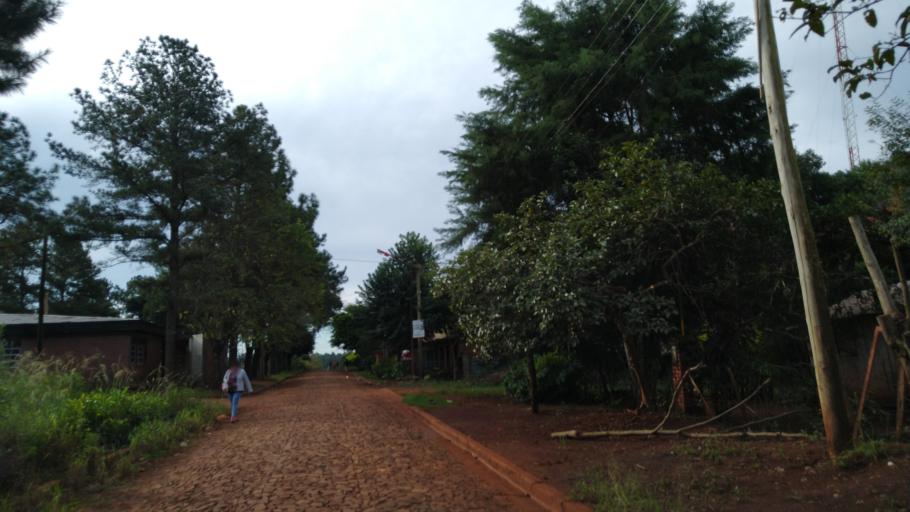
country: AR
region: Misiones
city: Capiovi
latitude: -26.9446
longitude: -55.0955
